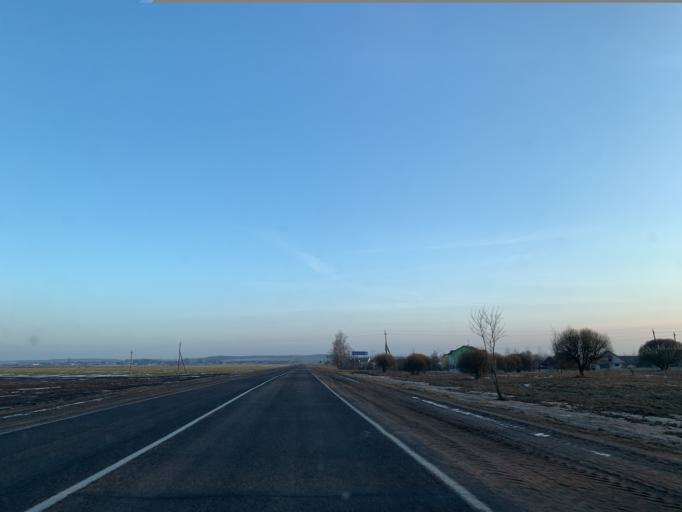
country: BY
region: Minsk
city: Haradzyeya
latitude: 53.3183
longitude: 26.5601
